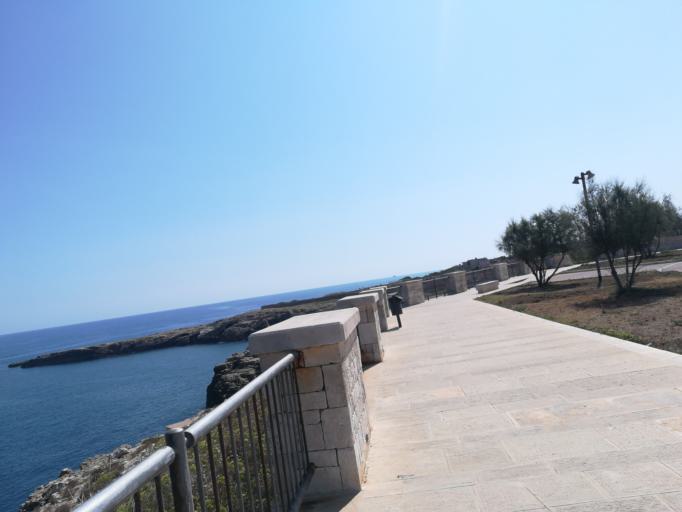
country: IT
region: Apulia
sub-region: Provincia di Bari
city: Polignano a Mare
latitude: 40.9928
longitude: 17.2322
